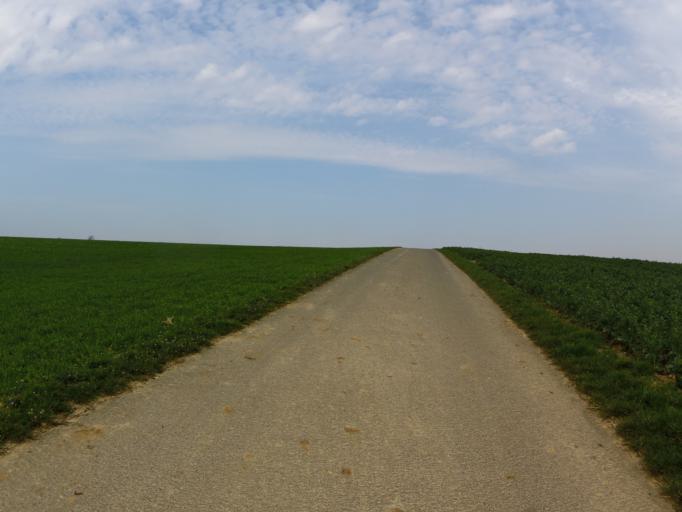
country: DE
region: Bavaria
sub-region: Regierungsbezirk Unterfranken
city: Biebelried
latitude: 49.7848
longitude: 10.1030
